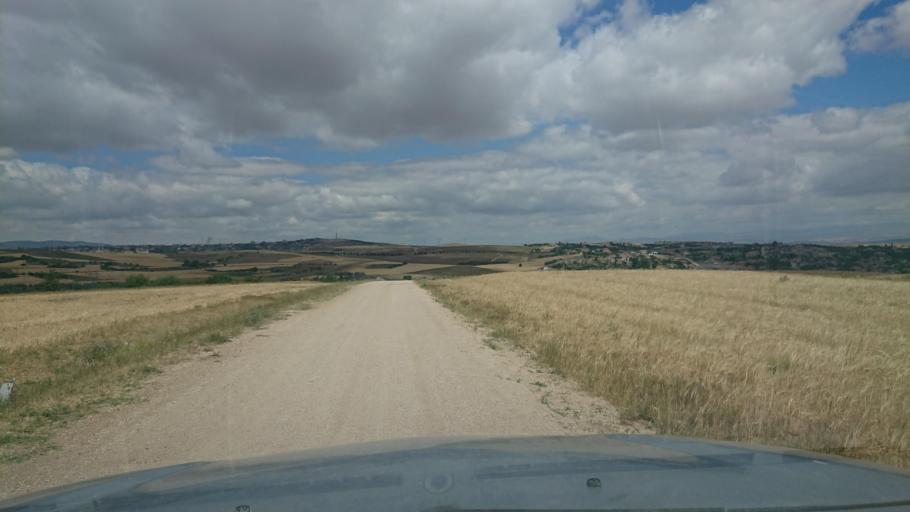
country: TR
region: Aksaray
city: Agacoren
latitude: 38.8562
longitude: 33.9502
